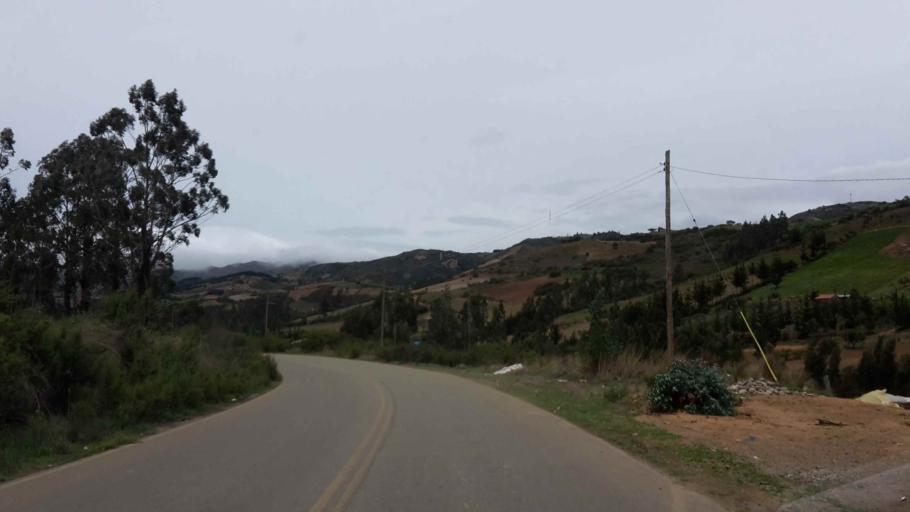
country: BO
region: Cochabamba
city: Totora
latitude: -17.6960
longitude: -65.2143
